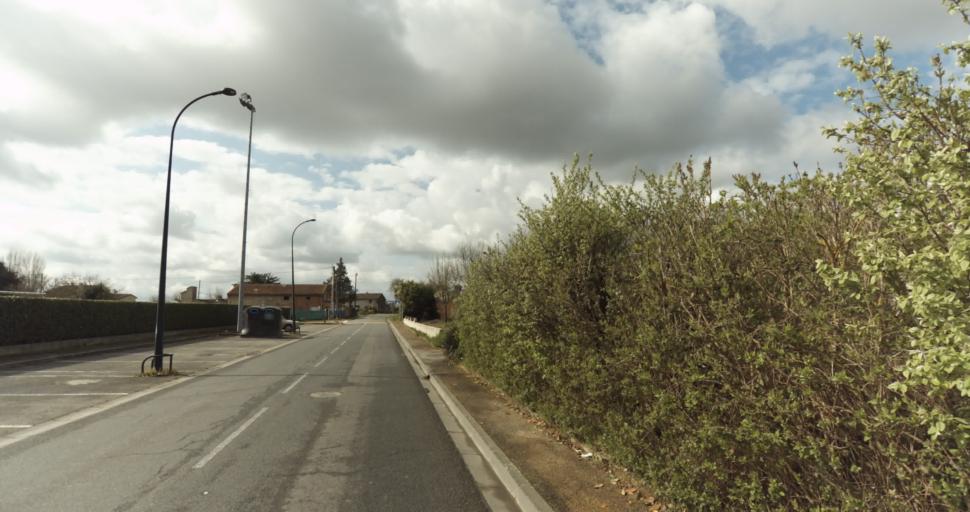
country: FR
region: Midi-Pyrenees
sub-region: Departement de la Haute-Garonne
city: Auterive
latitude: 43.3440
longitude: 1.4694
